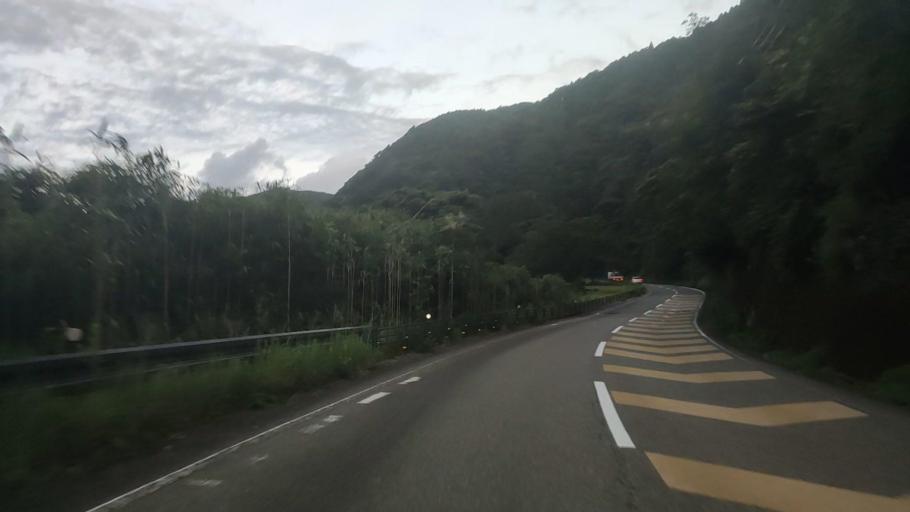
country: JP
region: Wakayama
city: Shingu
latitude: 33.7588
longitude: 135.9196
